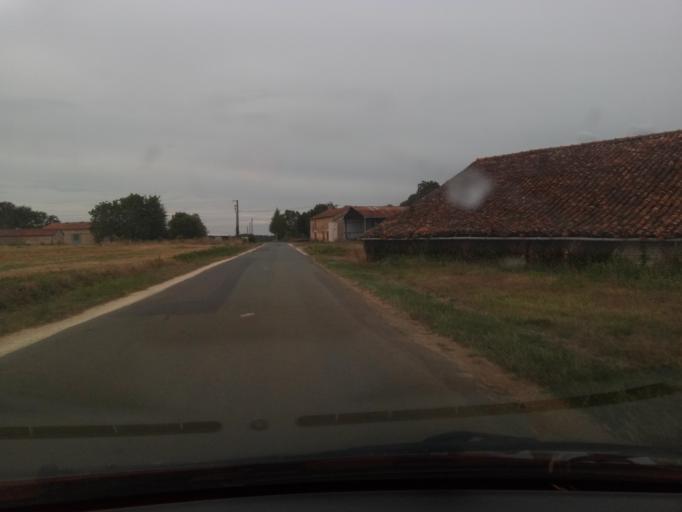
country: FR
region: Poitou-Charentes
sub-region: Departement de la Vienne
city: Saint-Savin
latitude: 46.5378
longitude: 0.7814
